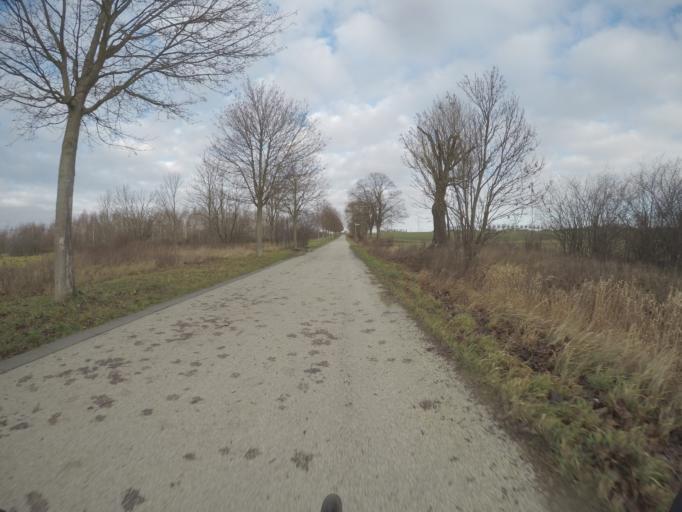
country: DE
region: Berlin
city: Wartenberg
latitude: 52.5882
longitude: 13.5046
